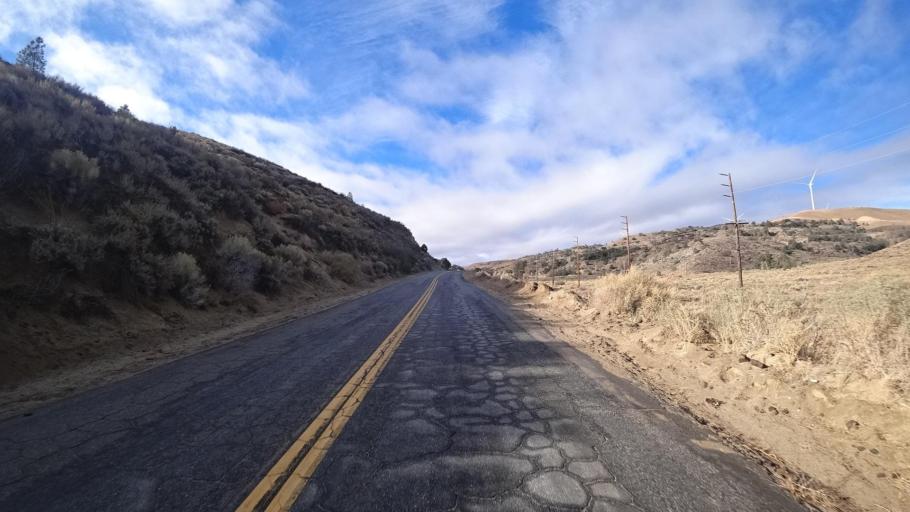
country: US
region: California
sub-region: Kern County
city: Tehachapi
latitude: 35.0866
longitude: -118.3199
